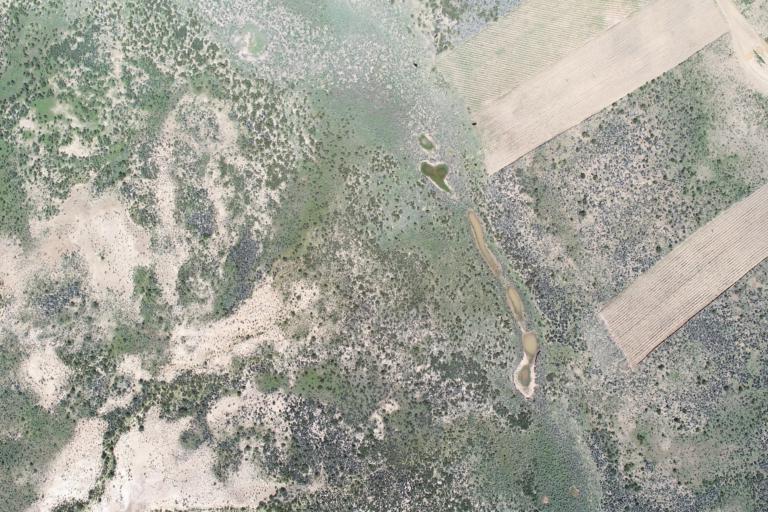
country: BO
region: La Paz
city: Curahuara de Carangas
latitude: -17.2965
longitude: -68.5170
